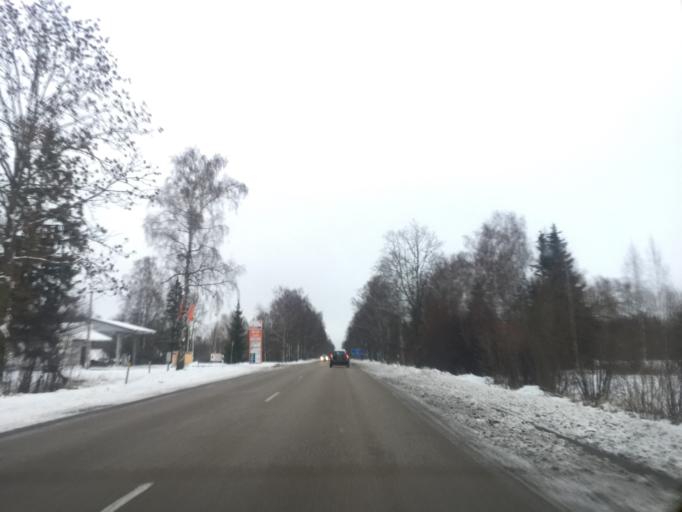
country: LV
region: Karsava
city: Karsava
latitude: 56.7741
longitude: 27.6875
